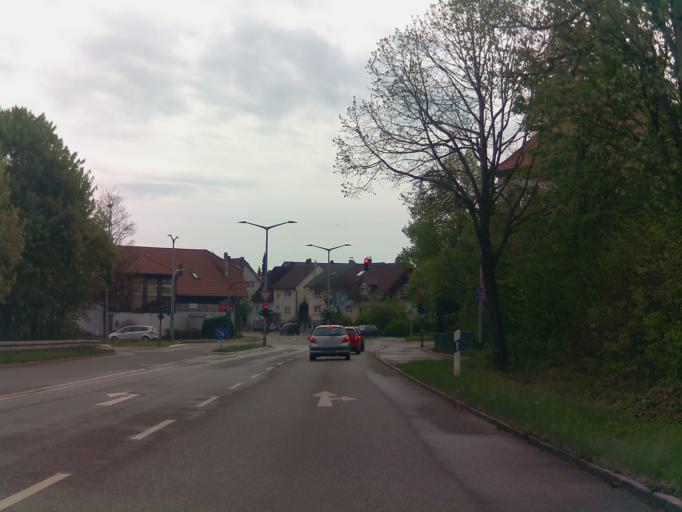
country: DE
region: Baden-Wuerttemberg
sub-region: Freiburg Region
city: Villingen-Schwenningen
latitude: 48.0662
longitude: 8.5242
